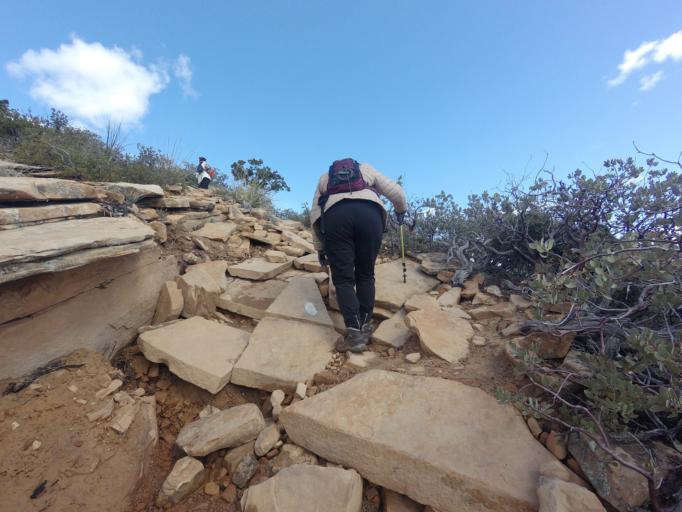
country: US
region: Arizona
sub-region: Yavapai County
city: West Sedona
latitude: 34.9105
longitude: -111.8766
